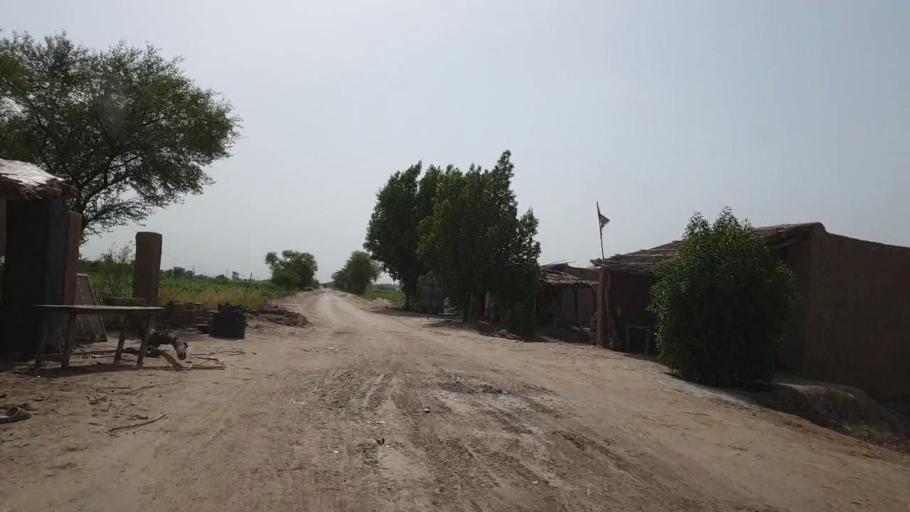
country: PK
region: Sindh
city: Bandhi
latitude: 26.5385
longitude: 68.4029
